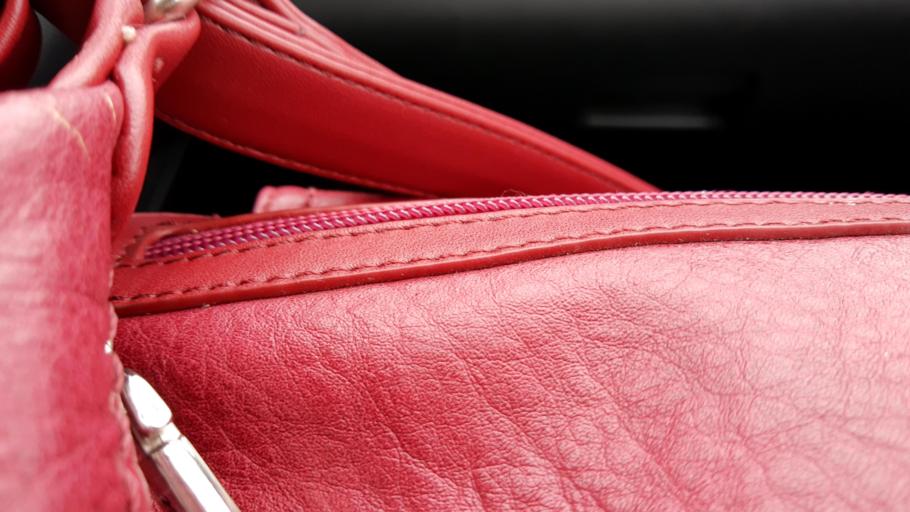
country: RU
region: Bashkortostan
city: Iglino
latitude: 54.7549
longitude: 56.3594
